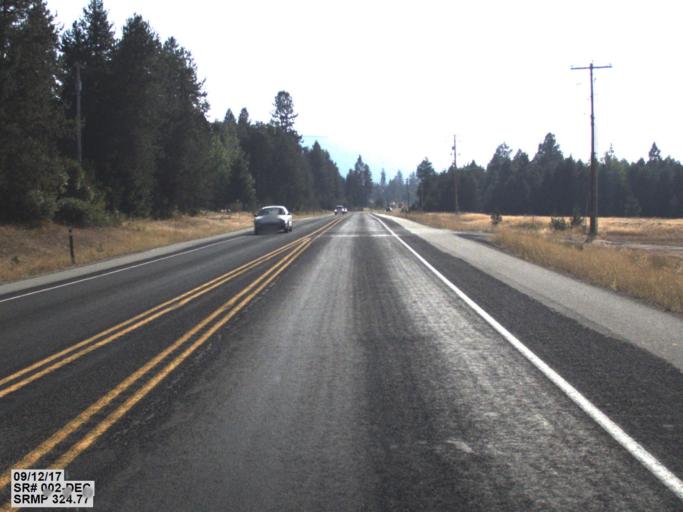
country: US
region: Washington
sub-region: Pend Oreille County
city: Newport
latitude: 48.1162
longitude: -117.2134
